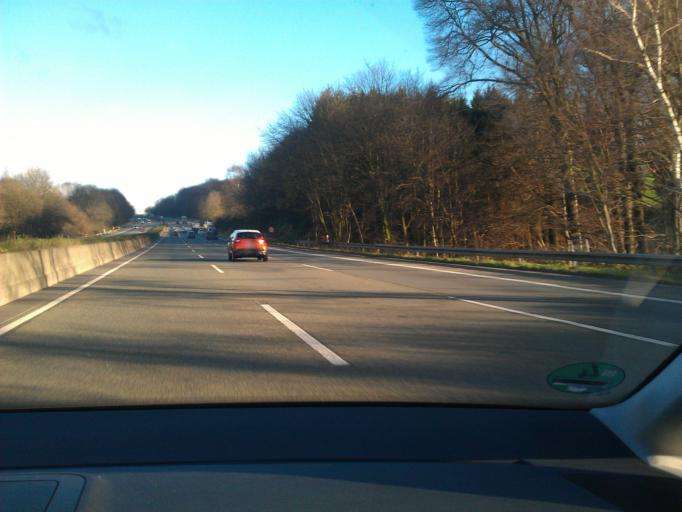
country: DE
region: North Rhine-Westphalia
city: Burscheid
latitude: 51.0713
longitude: 7.0976
